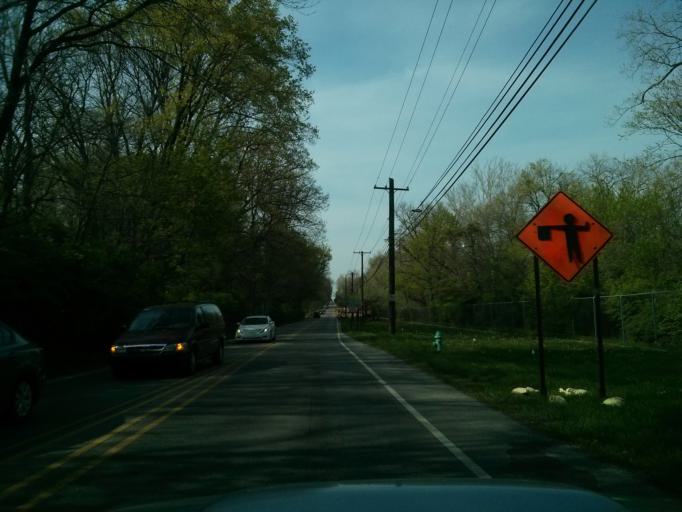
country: US
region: Indiana
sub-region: Marion County
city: Meridian Hills
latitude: 39.8913
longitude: -86.1458
